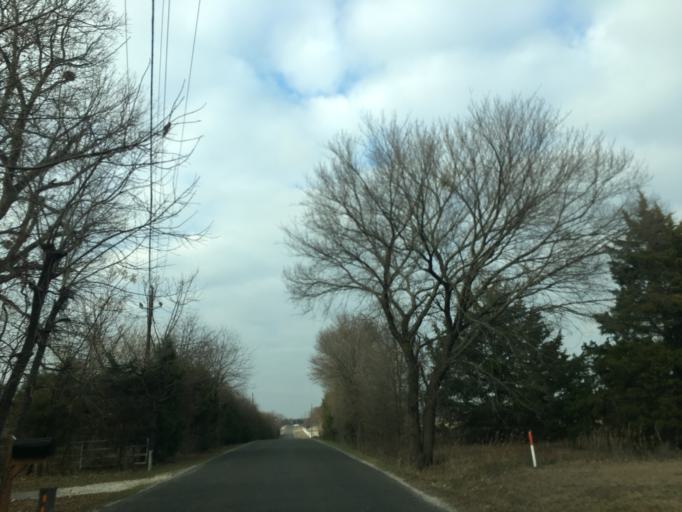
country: US
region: Texas
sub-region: Ellis County
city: Red Oak
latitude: 32.4800
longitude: -96.7890
